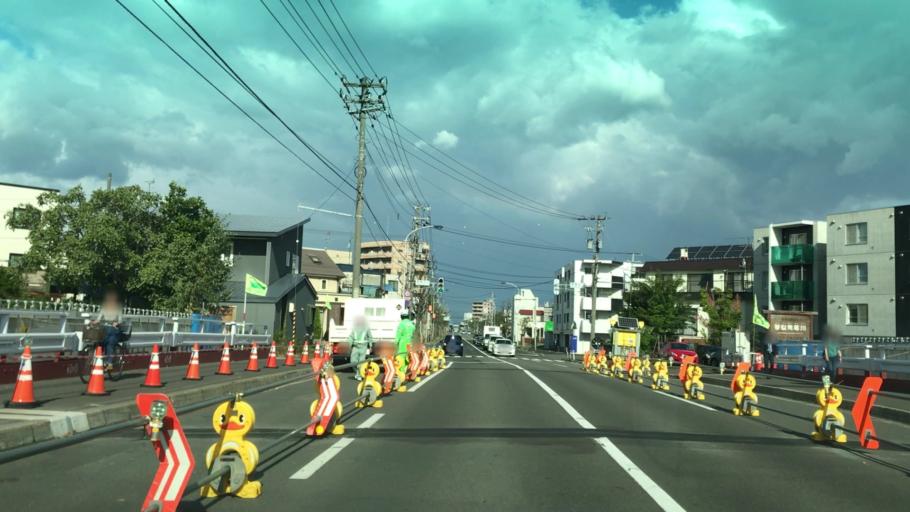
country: JP
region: Hokkaido
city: Sapporo
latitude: 43.0829
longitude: 141.3015
